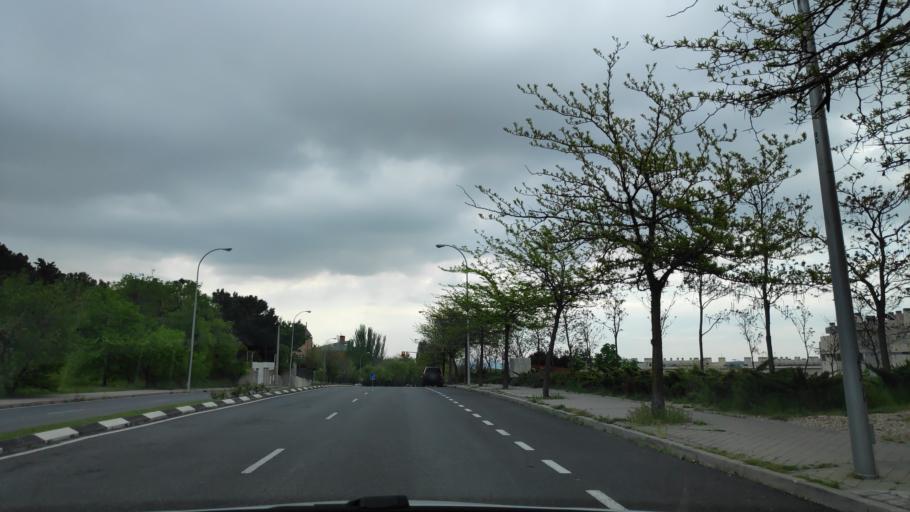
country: ES
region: Madrid
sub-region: Provincia de Madrid
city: Pozuelo de Alarcon
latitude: 40.4630
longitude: -3.7952
